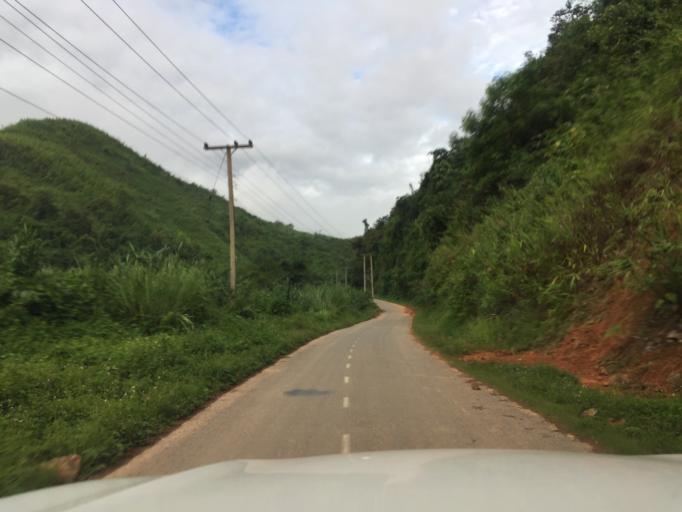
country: LA
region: Phongsali
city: Khoa
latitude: 21.1031
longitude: 102.2942
